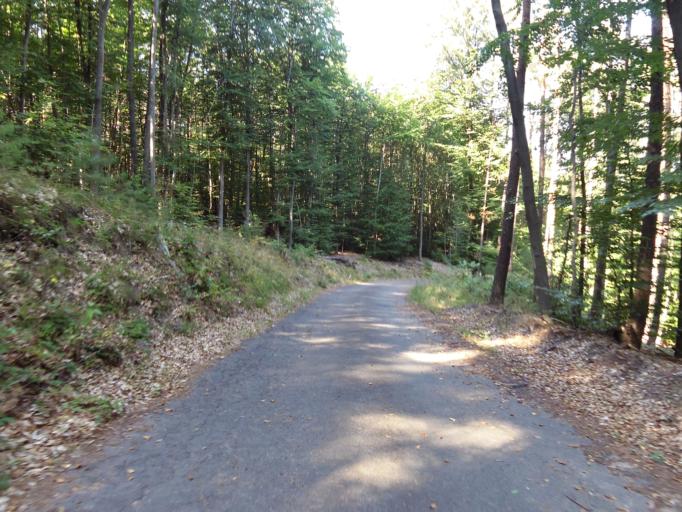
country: DE
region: Rheinland-Pfalz
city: Neidenfels
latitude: 49.4304
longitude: 8.0564
